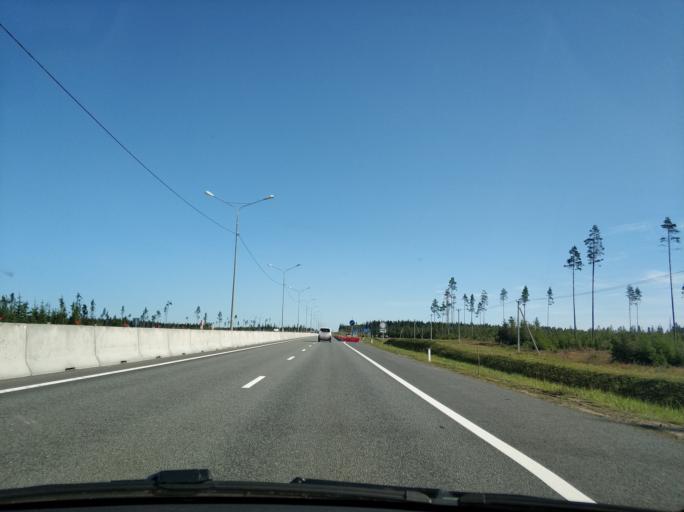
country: RU
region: Leningrad
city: Sosnovo
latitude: 60.4724
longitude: 30.1960
